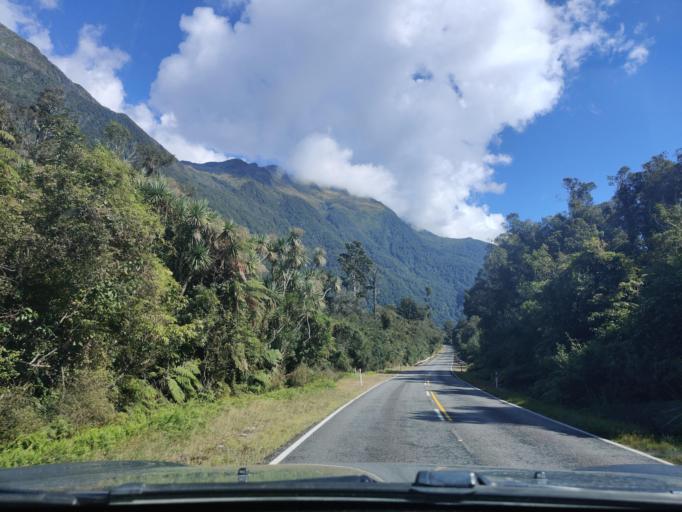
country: NZ
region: Otago
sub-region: Queenstown-Lakes District
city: Wanaka
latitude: -43.9696
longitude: 169.1802
